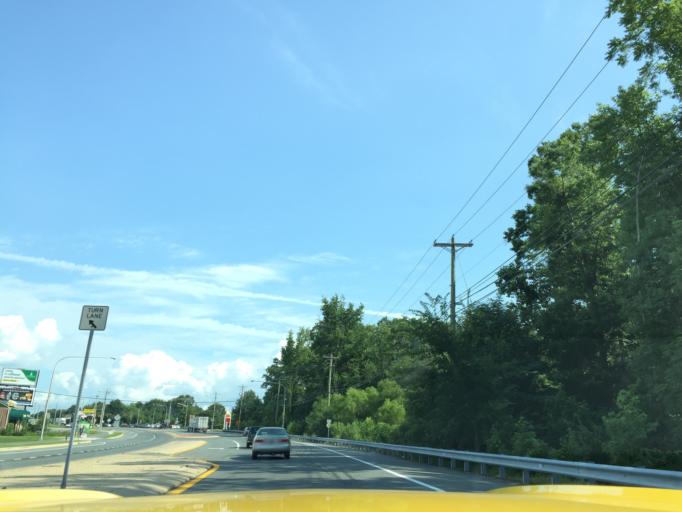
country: US
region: Delaware
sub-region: New Castle County
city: Newport
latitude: 39.6790
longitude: -75.6286
